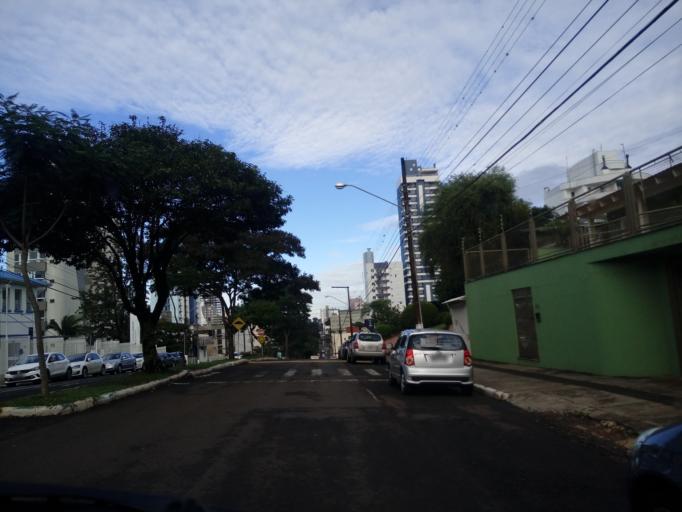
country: BR
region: Santa Catarina
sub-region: Chapeco
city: Chapeco
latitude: -27.1034
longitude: -52.6087
